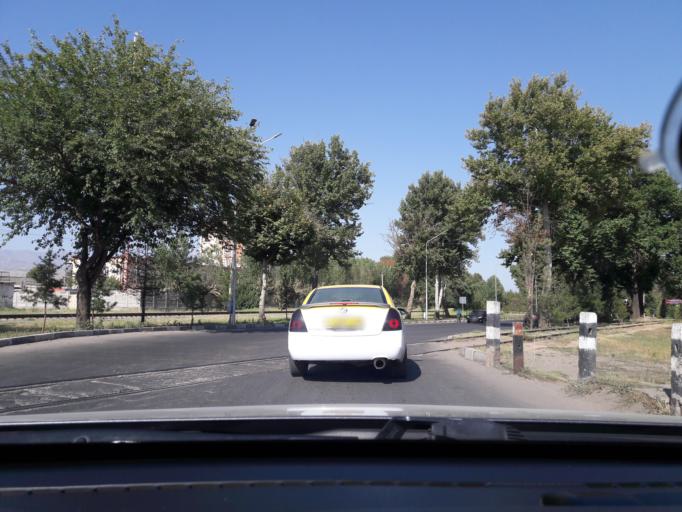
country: TJ
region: Dushanbe
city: Dushanbe
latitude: 38.5693
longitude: 68.7588
